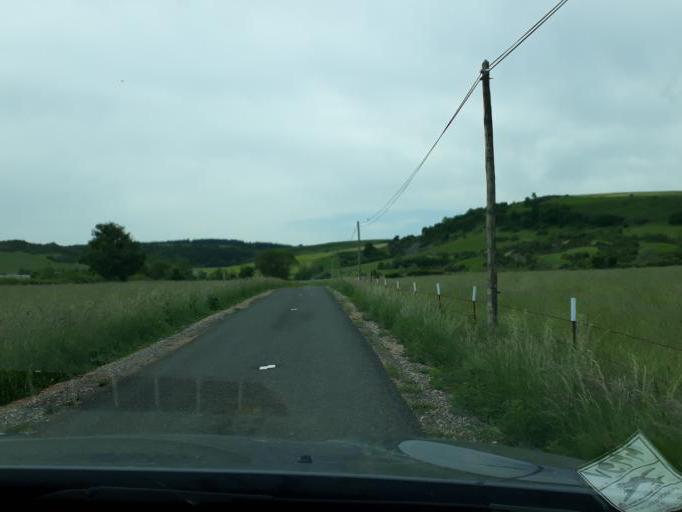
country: FR
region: Languedoc-Roussillon
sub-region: Departement de l'Herault
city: Lodeve
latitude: 43.8277
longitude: 3.2674
